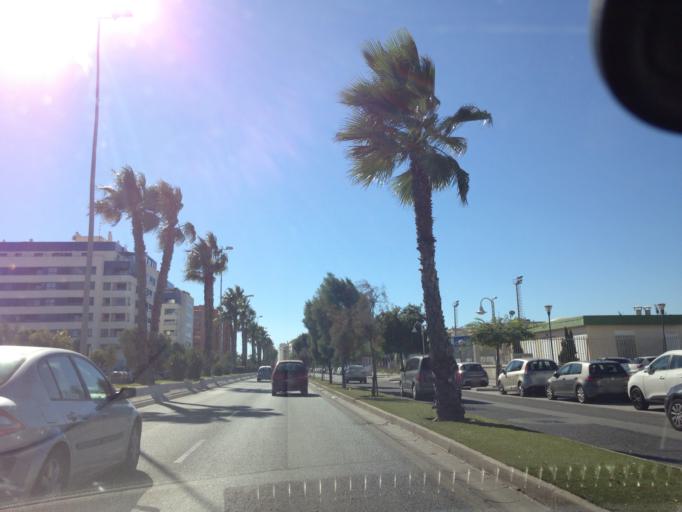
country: ES
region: Andalusia
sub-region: Provincia de Malaga
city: Malaga
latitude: 36.6974
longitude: -4.4382
